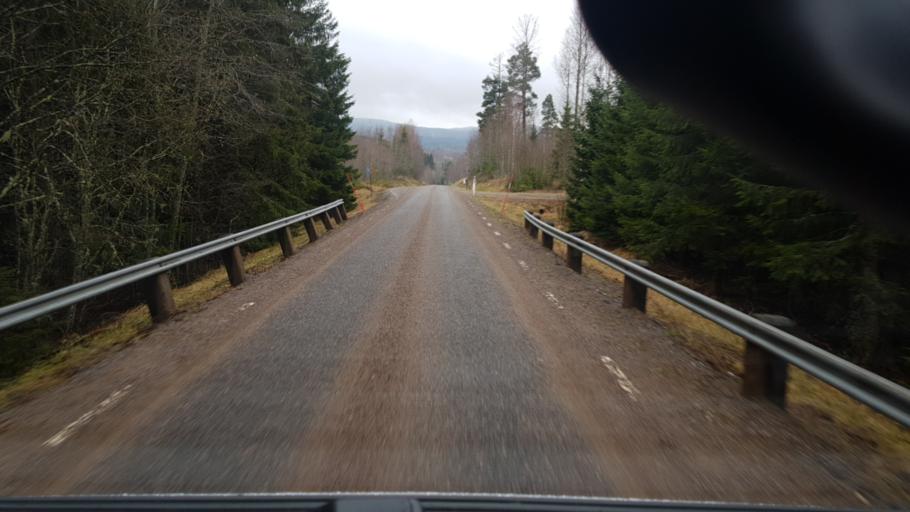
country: SE
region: Vaermland
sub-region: Eda Kommun
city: Charlottenberg
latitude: 59.9798
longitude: 12.4125
